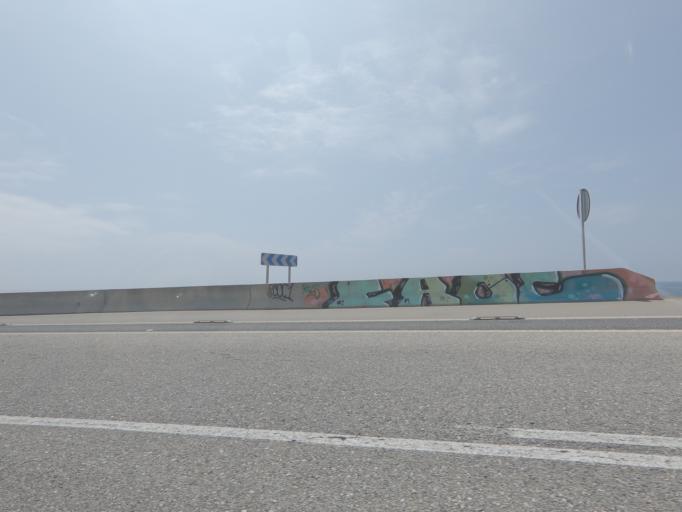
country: ES
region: Galicia
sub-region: Provincia de Pontevedra
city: Baiona
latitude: 42.1037
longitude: -8.8980
